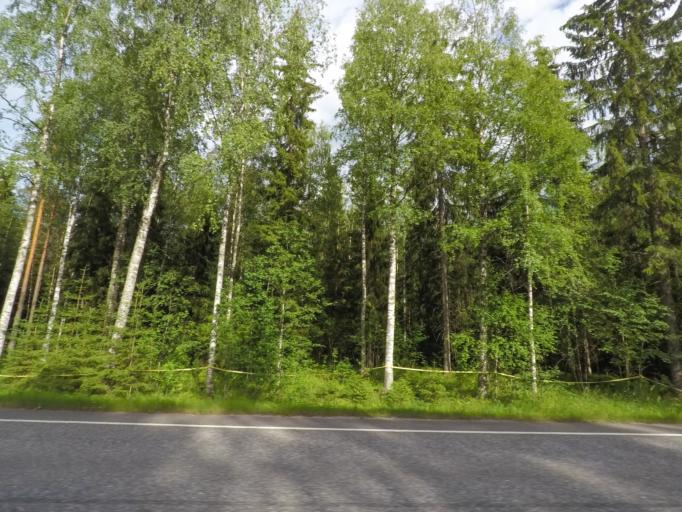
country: FI
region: Paijanne Tavastia
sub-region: Lahti
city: Hollola
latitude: 60.8355
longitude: 25.4922
